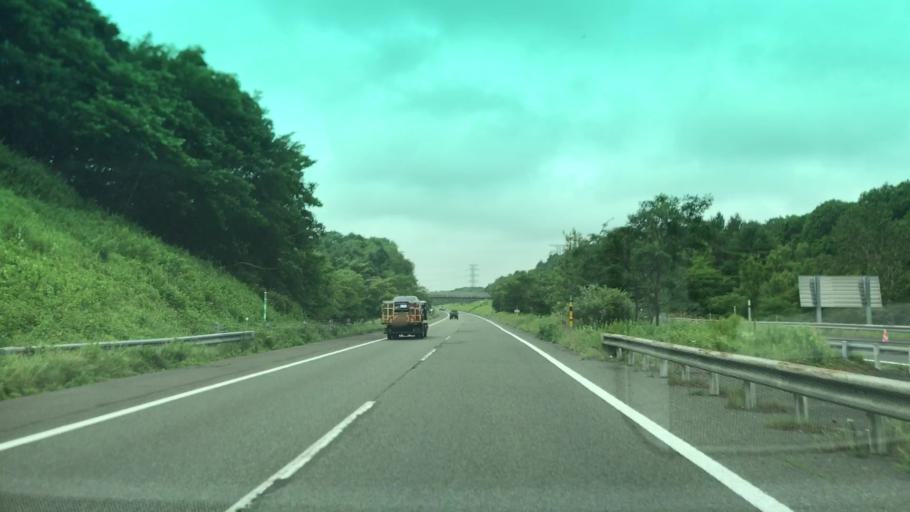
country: JP
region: Hokkaido
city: Chitose
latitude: 42.7289
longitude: 141.6530
